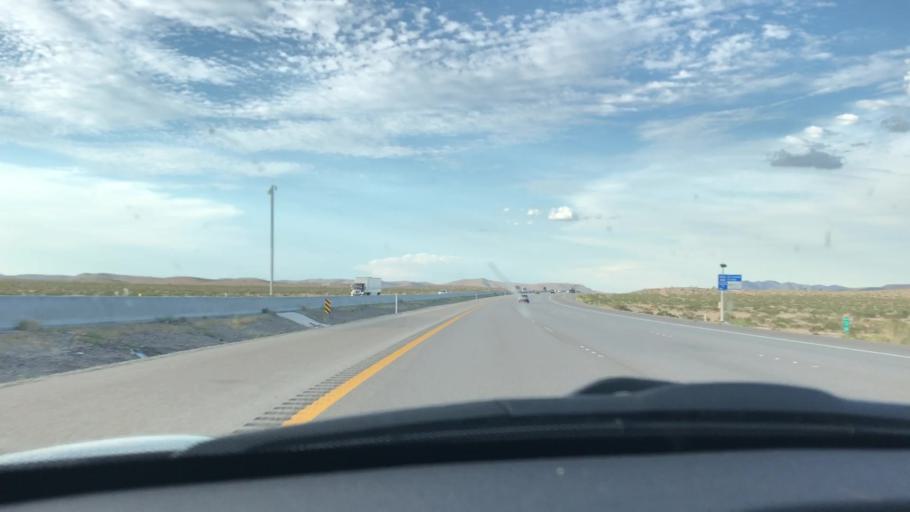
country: US
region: Nevada
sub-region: Clark County
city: Enterprise
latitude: 35.8224
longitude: -115.2976
